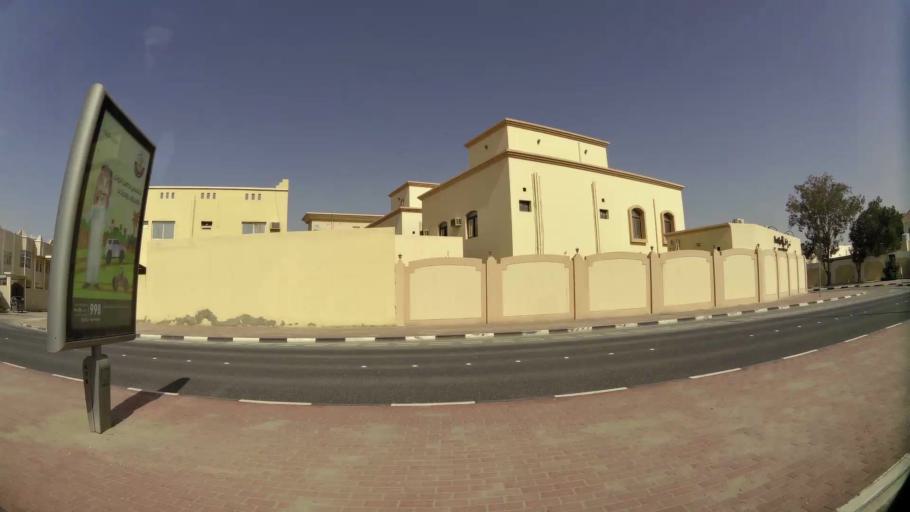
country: QA
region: Baladiyat Umm Salal
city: Umm Salal Muhammad
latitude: 25.3680
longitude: 51.4354
